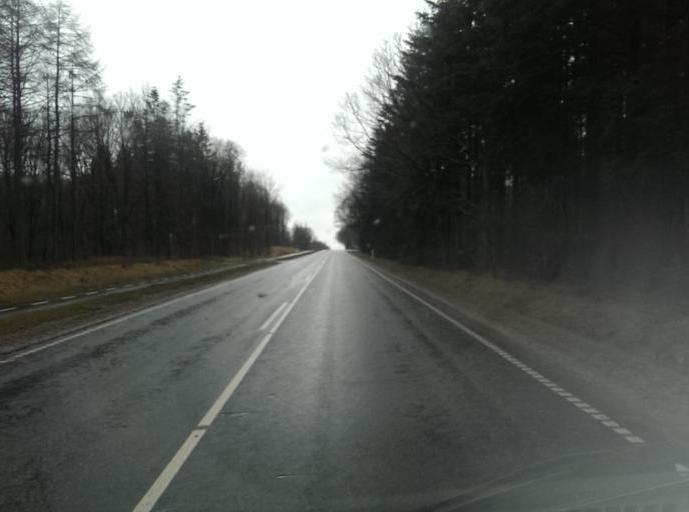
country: DK
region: Central Jutland
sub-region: Ringkobing-Skjern Kommune
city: Skjern
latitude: 55.9881
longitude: 8.4540
